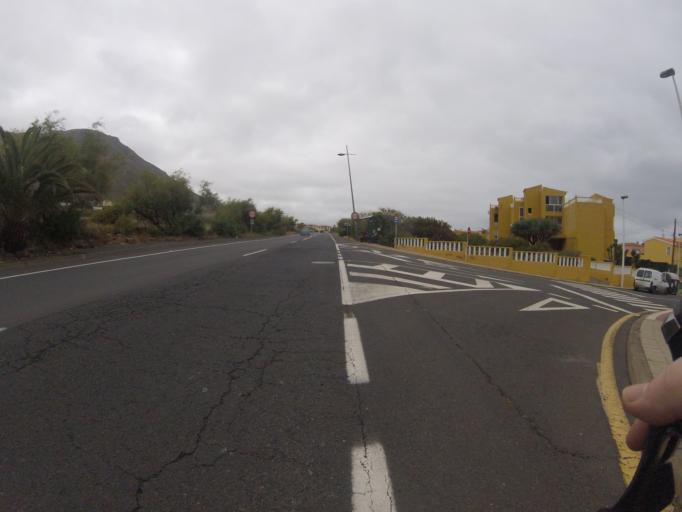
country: ES
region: Canary Islands
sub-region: Provincia de Santa Cruz de Tenerife
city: Tegueste
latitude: 28.5508
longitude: -16.3488
